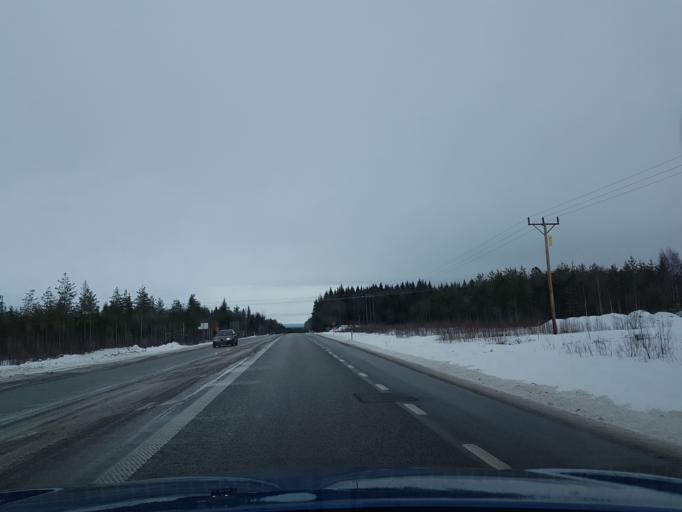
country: SE
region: Dalarna
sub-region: Mora Kommun
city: Mora
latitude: 61.0212
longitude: 14.5888
